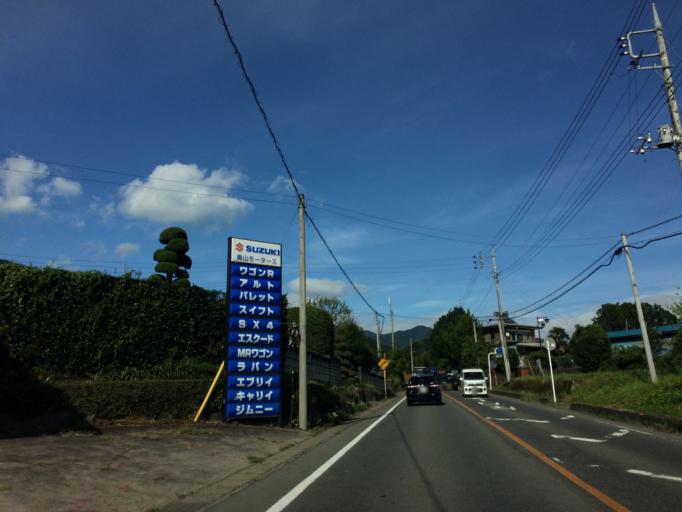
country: JP
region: Gunma
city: Shibukawa
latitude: 36.5446
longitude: 138.9360
